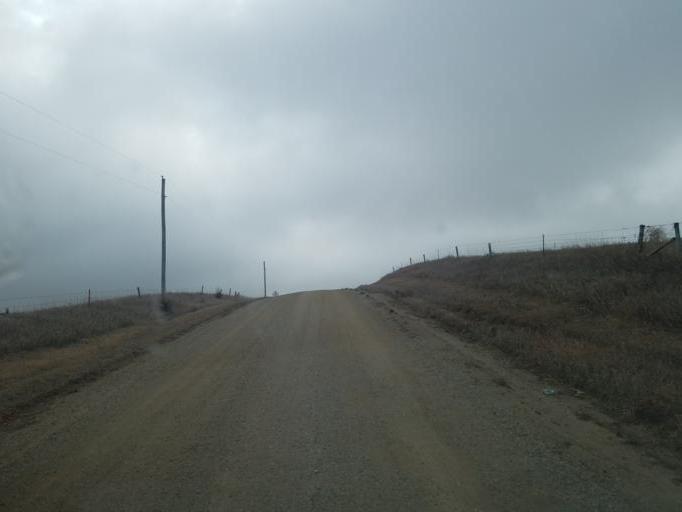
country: US
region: Nebraska
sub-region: Knox County
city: Creighton
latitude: 42.5058
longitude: -97.7984
